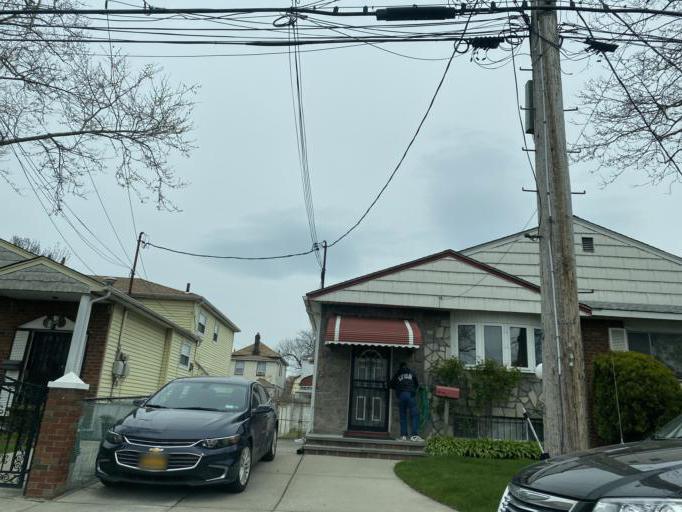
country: US
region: New York
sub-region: Queens County
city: Jamaica
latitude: 40.6687
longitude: -73.7771
